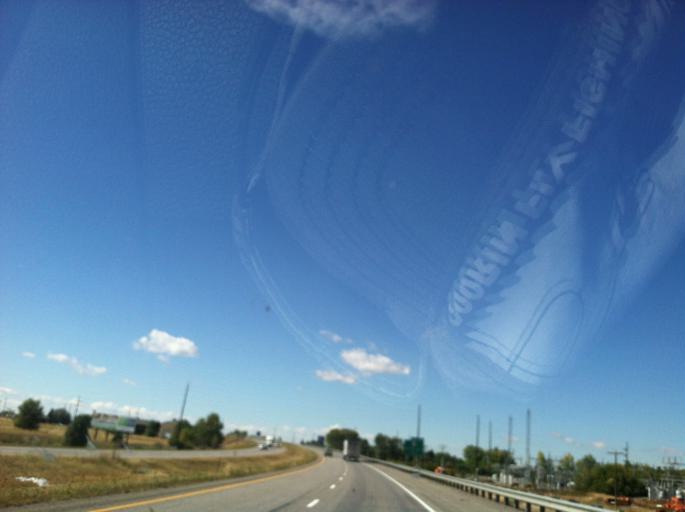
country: US
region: Montana
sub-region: Gallatin County
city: Bozeman
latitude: 45.6898
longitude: -111.0206
